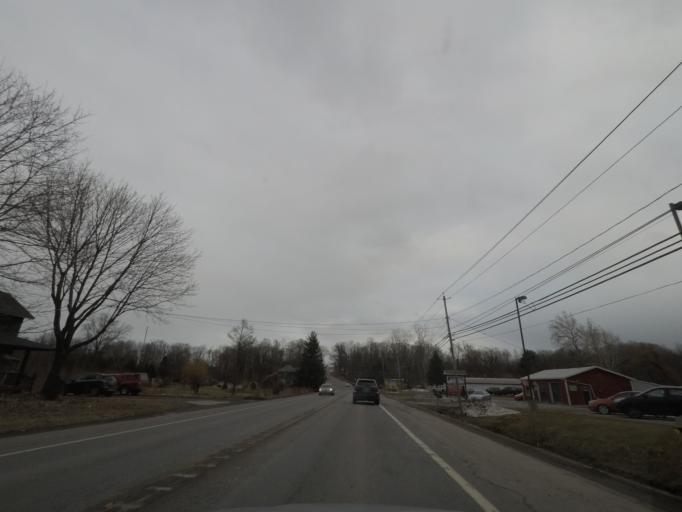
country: US
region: New York
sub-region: Madison County
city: Wampsville
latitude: 43.0757
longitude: -75.6990
